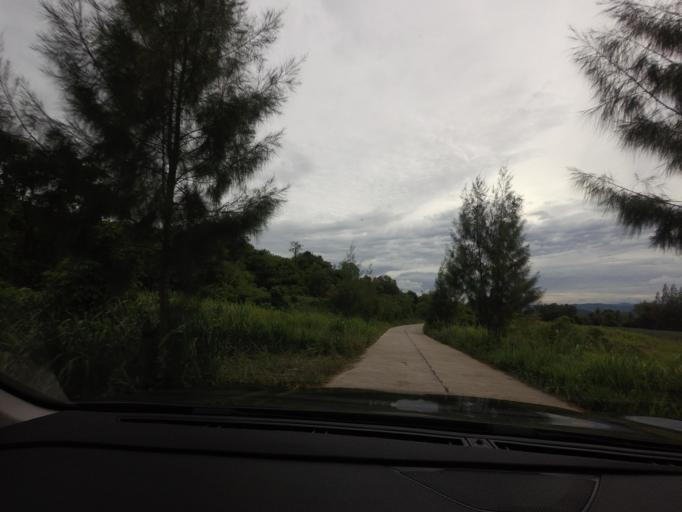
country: TH
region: Prachuap Khiri Khan
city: Hua Hin
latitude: 12.4830
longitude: 99.9424
